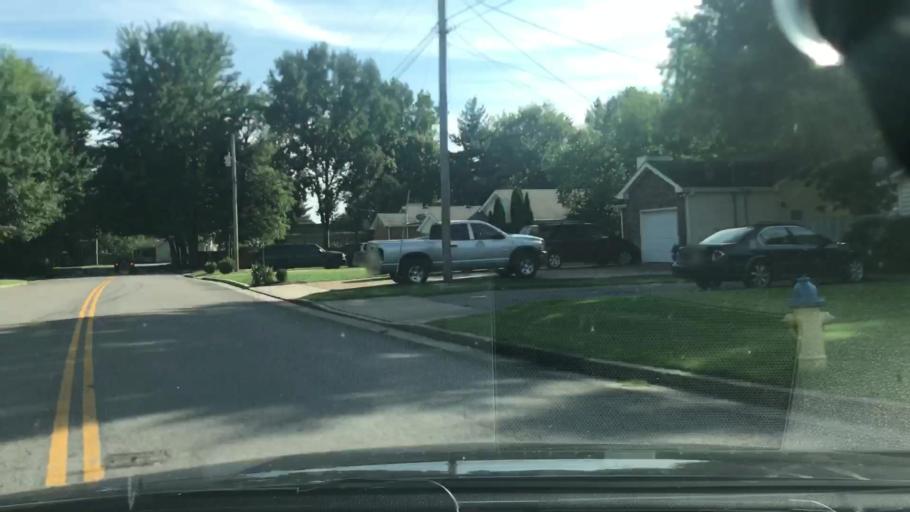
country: US
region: Tennessee
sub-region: Williamson County
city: Franklin
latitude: 35.9317
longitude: -86.8821
